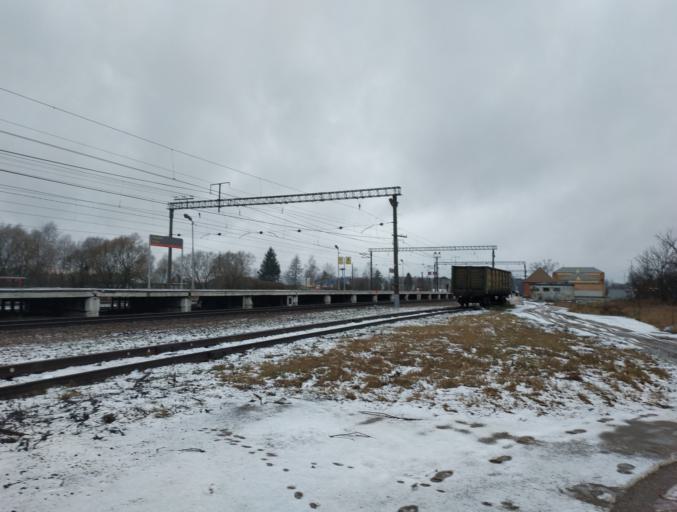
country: RU
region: Moskovskaya
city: Taldom
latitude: 56.7215
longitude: 37.5284
